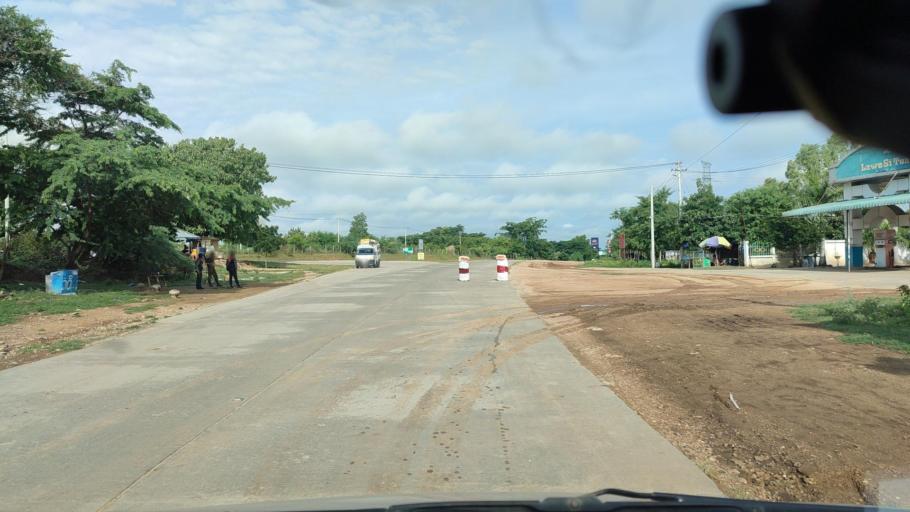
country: MM
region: Mandalay
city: Meiktila
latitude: 20.9406
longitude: 95.7796
